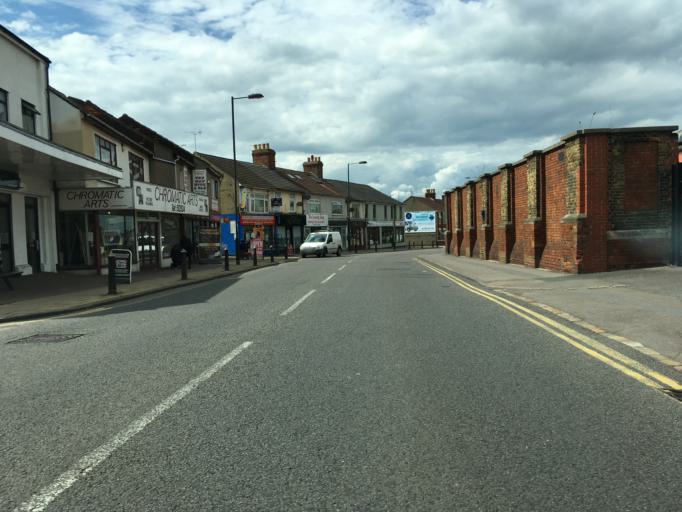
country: GB
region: England
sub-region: Borough of Swindon
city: Swindon
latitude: 51.5628
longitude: -1.7994
